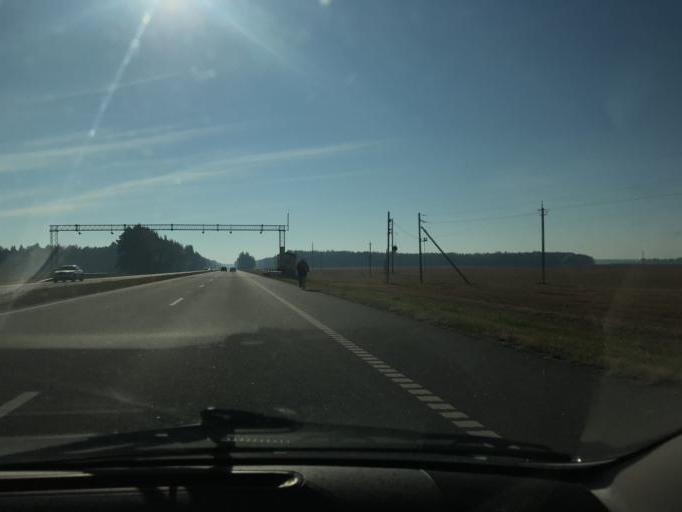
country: BY
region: Minsk
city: Slutsk
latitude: 53.3198
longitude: 27.5350
